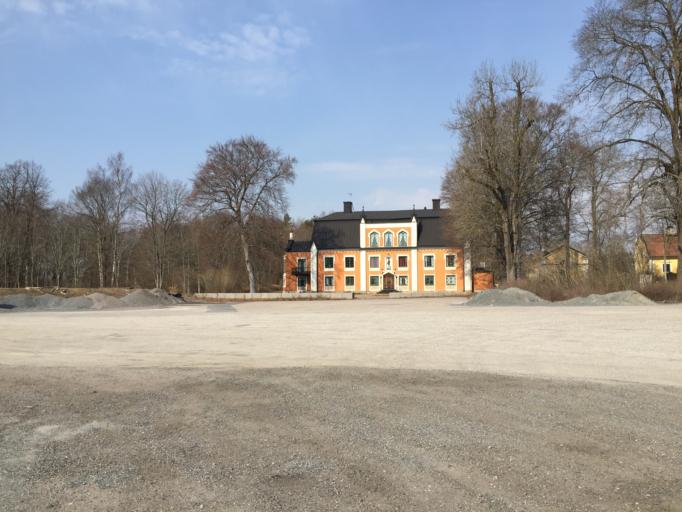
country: SE
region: Soedermanland
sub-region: Flens Kommun
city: Halleforsnas
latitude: 59.1525
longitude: 16.4887
